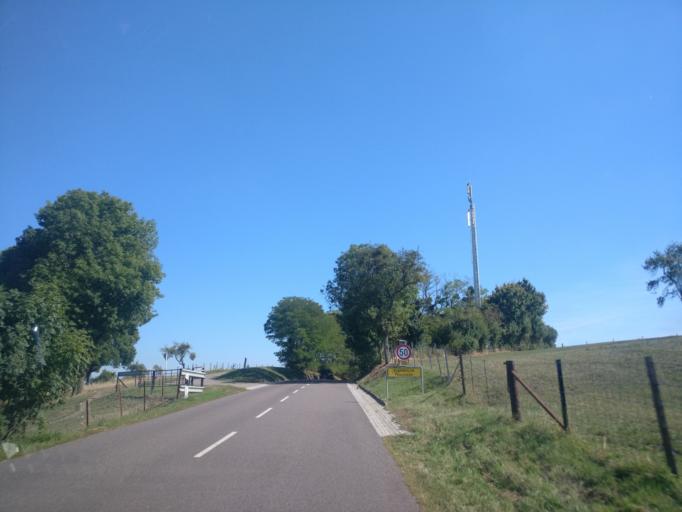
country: LU
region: Grevenmacher
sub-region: Canton de Grevenmacher
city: Flaxweiler
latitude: 49.6684
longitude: 6.3350
